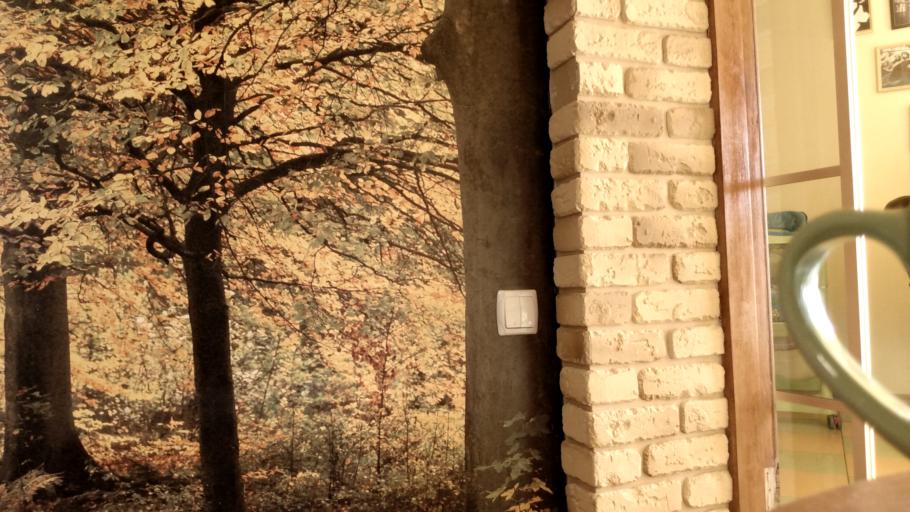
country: RU
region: Vologda
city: Imeni Zhelyabova
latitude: 58.8029
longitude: 36.8900
